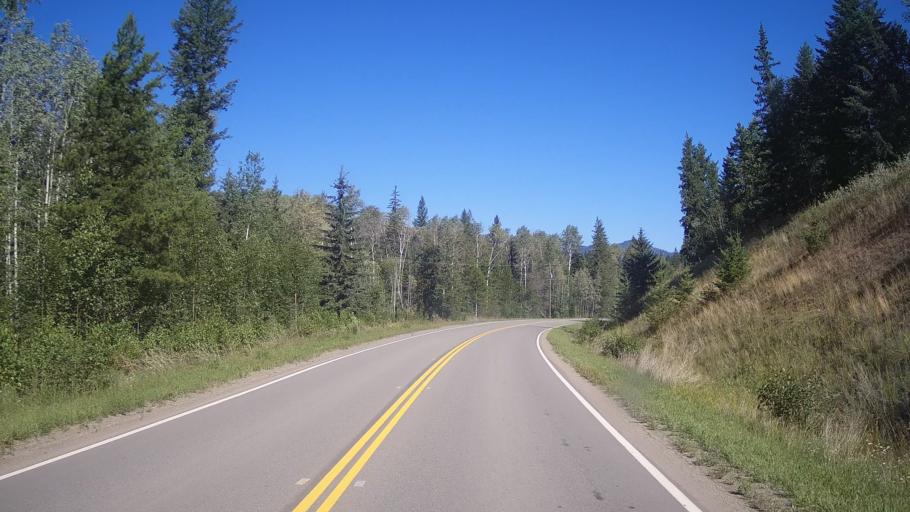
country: CA
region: British Columbia
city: Kamloops
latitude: 51.4404
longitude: -120.2111
